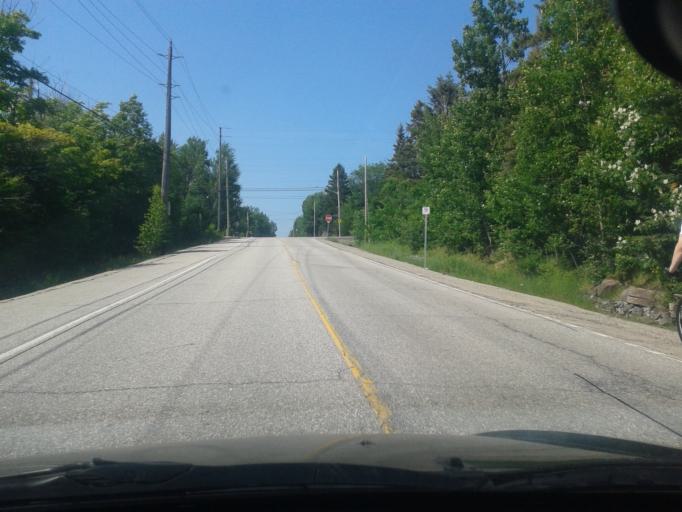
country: CA
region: Ontario
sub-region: Nipissing District
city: North Bay
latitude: 46.3462
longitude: -79.4872
